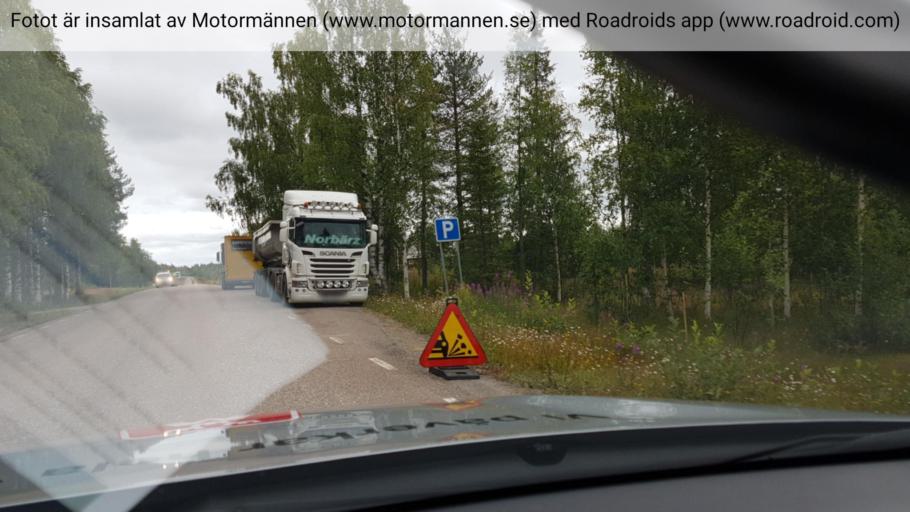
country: SE
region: Norrbotten
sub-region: Overkalix Kommun
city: OEverkalix
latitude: 67.0438
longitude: 22.0972
